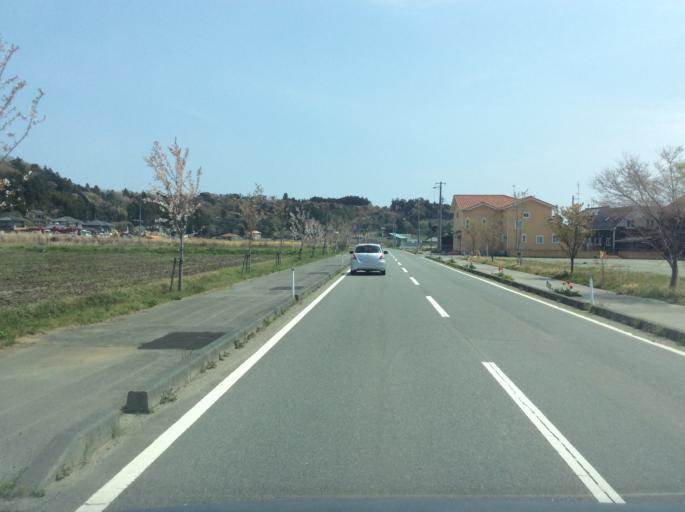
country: JP
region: Fukushima
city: Namie
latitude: 37.2762
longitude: 140.9999
